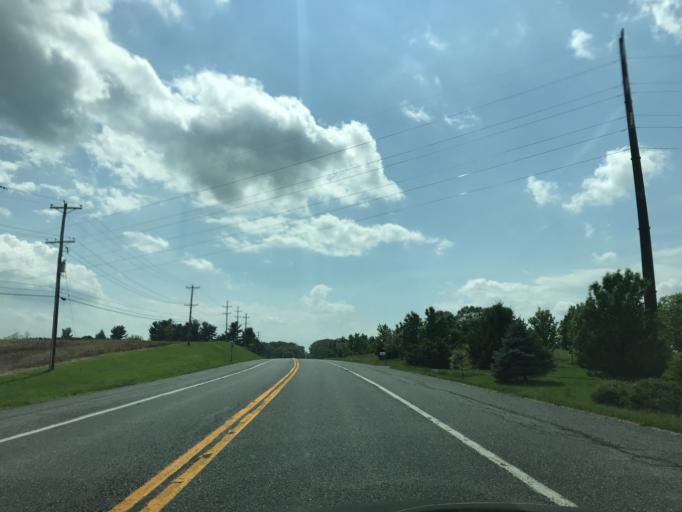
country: US
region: Pennsylvania
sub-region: York County
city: Susquehanna Trails
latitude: 39.6808
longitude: -76.3861
